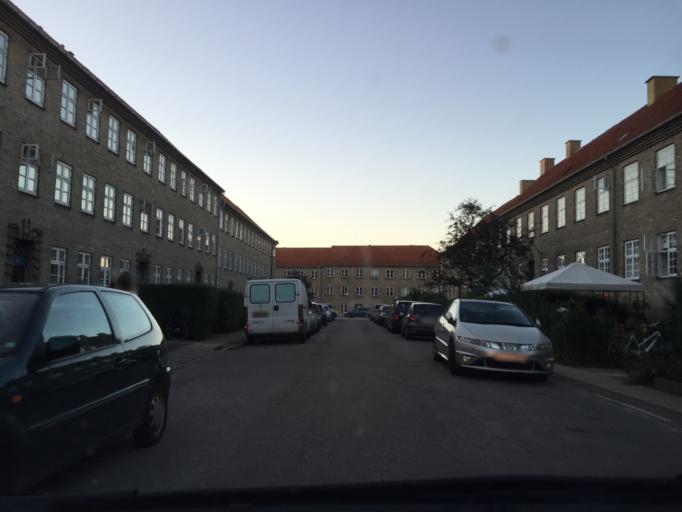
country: DK
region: Capital Region
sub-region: Frederiksberg Kommune
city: Frederiksberg
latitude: 55.7172
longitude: 12.5322
